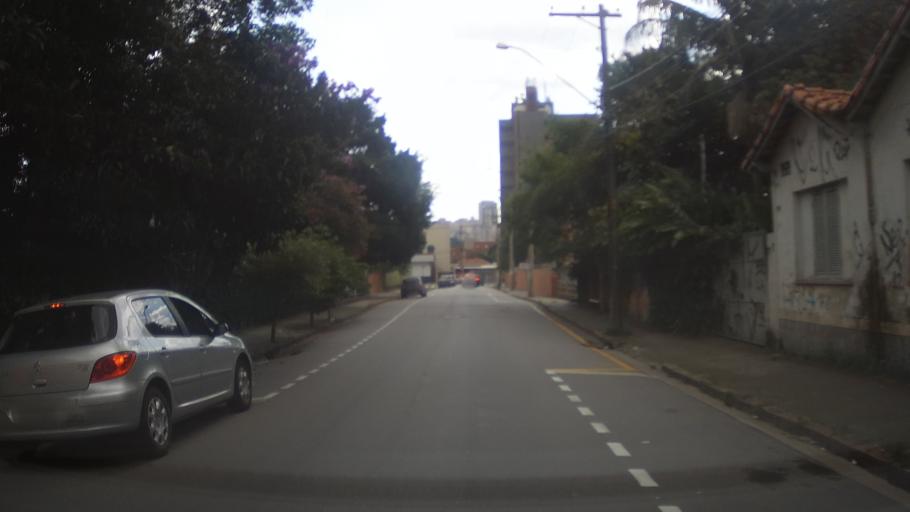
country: BR
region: Sao Paulo
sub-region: Jundiai
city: Jundiai
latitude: -23.2057
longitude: -46.8791
